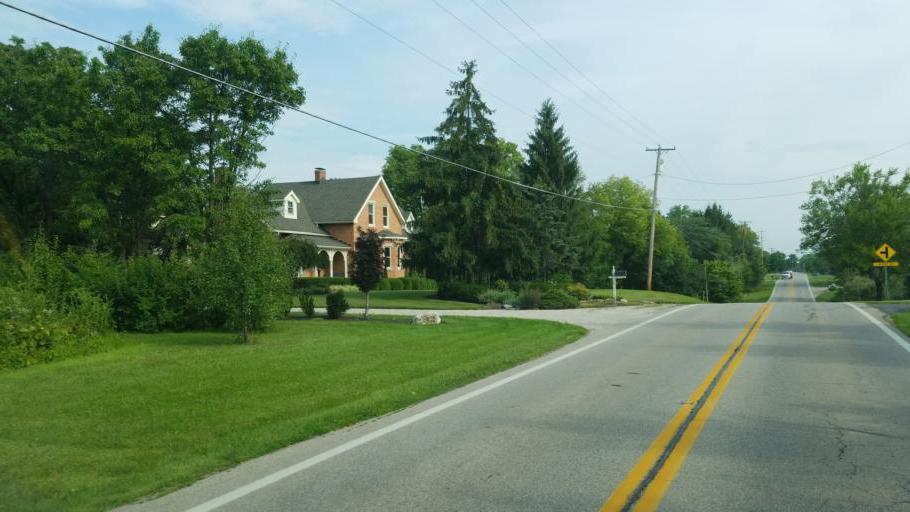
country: US
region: Ohio
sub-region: Delaware County
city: Powell
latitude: 40.2147
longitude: -83.1484
